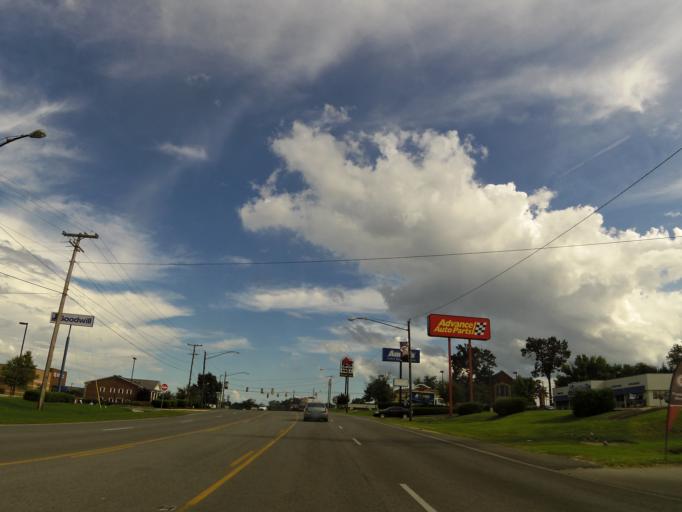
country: US
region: Kentucky
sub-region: Christian County
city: Hopkinsville
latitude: 36.8433
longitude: -87.4843
